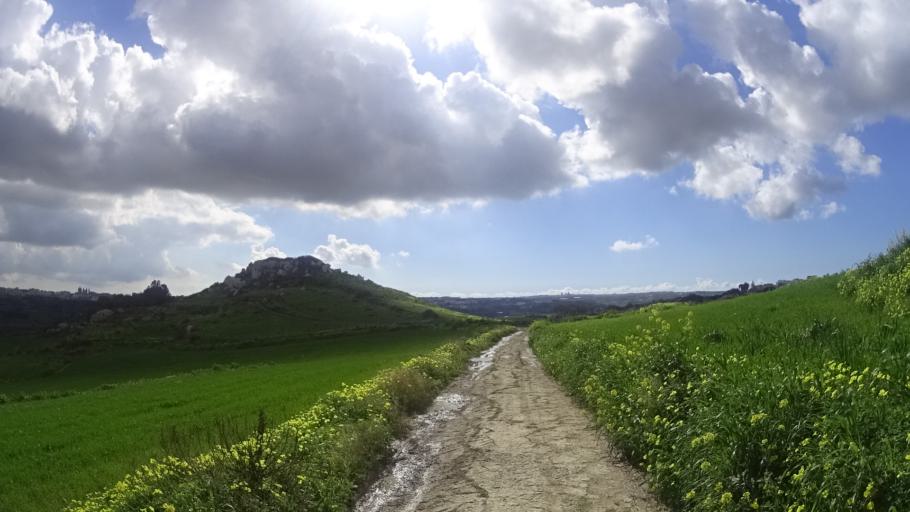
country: MT
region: L-Imtarfa
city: Imtarfa
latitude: 35.9007
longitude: 14.3843
